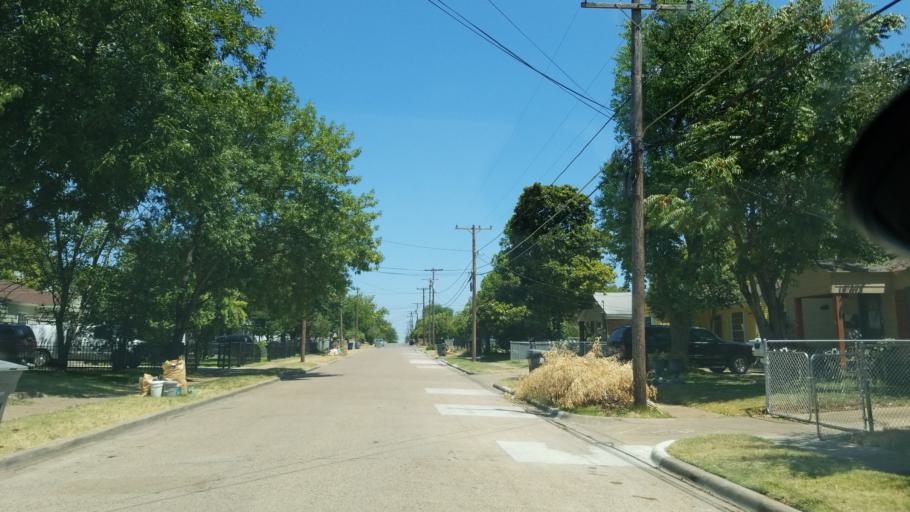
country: US
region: Texas
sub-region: Dallas County
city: Cockrell Hill
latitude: 32.7284
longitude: -96.8895
